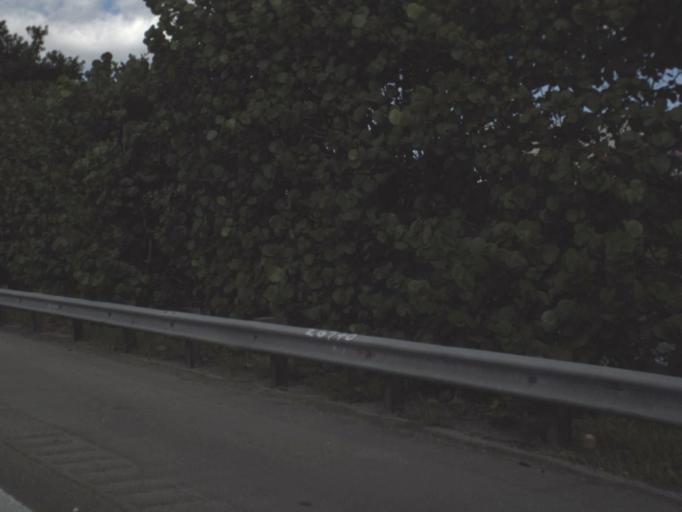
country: US
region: Florida
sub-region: Broward County
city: Davie
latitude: 26.0489
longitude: -80.2147
